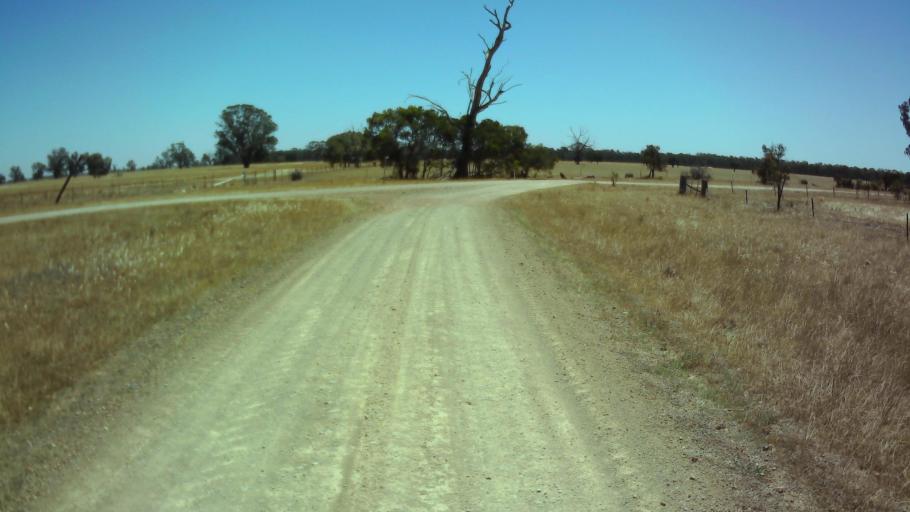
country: AU
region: New South Wales
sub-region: Weddin
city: Grenfell
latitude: -33.9854
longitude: 147.9280
